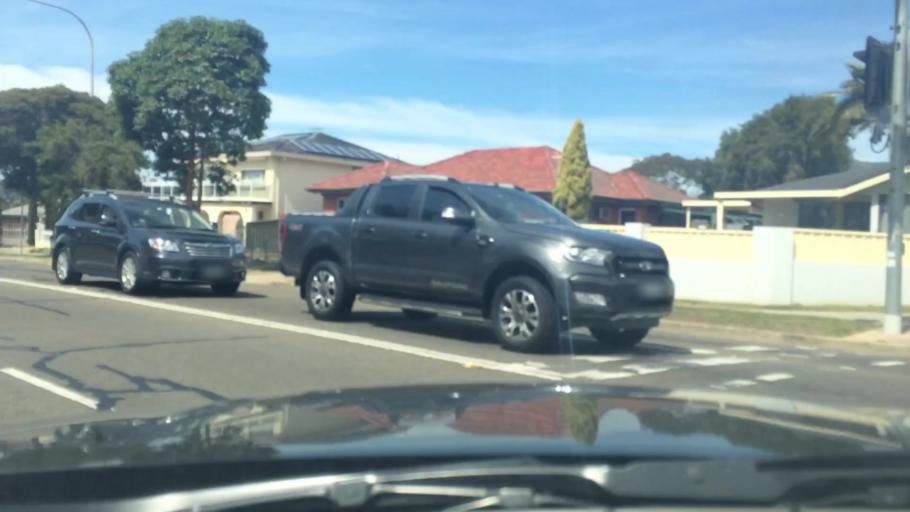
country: AU
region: New South Wales
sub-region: Fairfield
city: Cabramatta West
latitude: -33.8670
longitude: 150.8896
